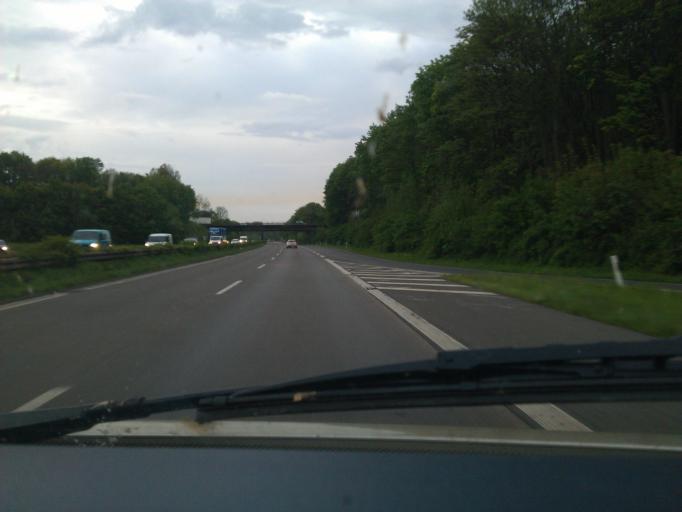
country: DE
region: North Rhine-Westphalia
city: Siersdorf
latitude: 50.8651
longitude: 6.2197
